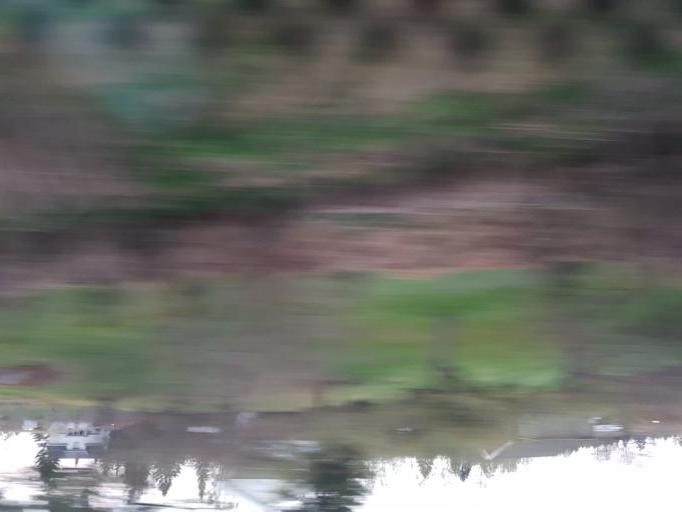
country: NO
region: Hedmark
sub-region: Ringsaker
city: Moelv
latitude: 60.9140
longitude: 10.7535
